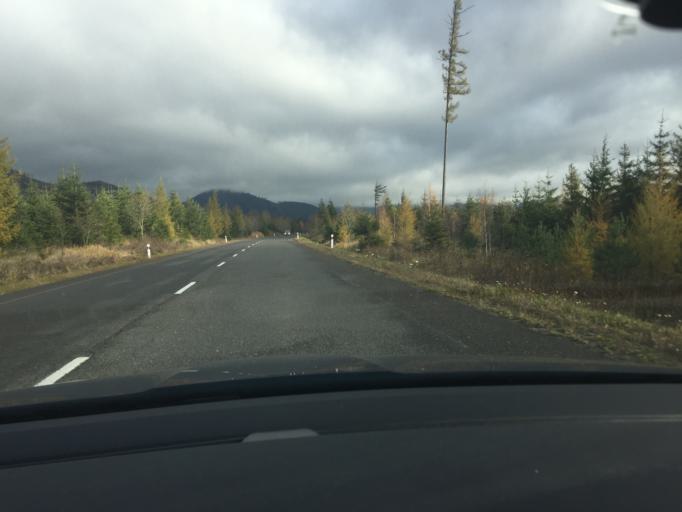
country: SK
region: Presovsky
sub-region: Okres Poprad
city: Nova Lesna
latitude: 49.1964
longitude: 20.3026
